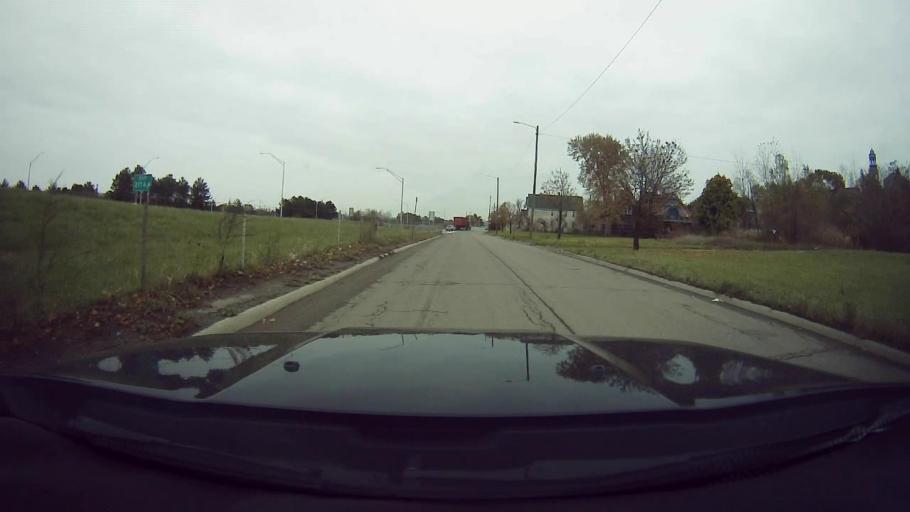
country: US
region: Michigan
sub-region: Wayne County
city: Hamtramck
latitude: 42.3716
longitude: -83.0490
